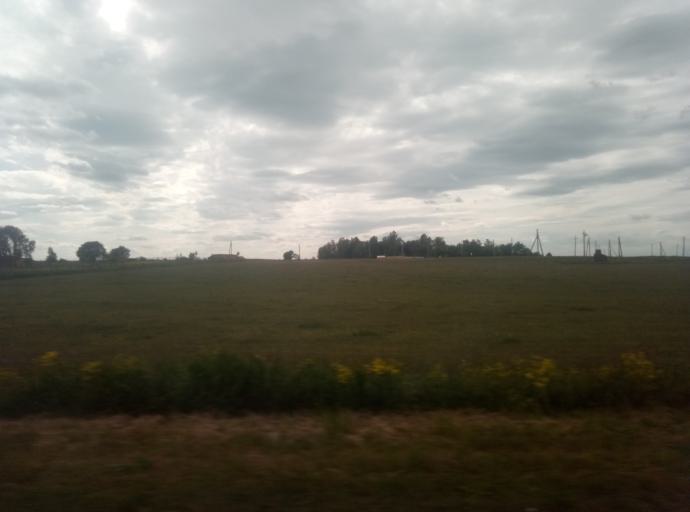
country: RU
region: Tula
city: Kireyevsk
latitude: 53.9617
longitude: 37.9374
